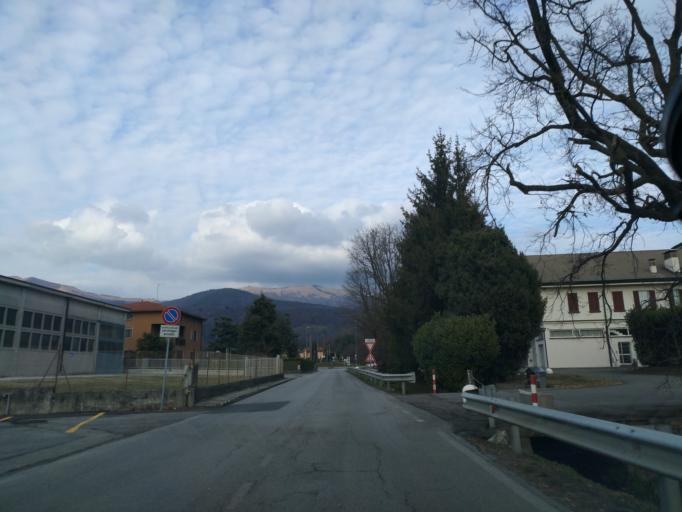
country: IT
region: Lombardy
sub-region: Provincia di Como
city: Albese Con Cassano
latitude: 45.7873
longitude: 9.1573
